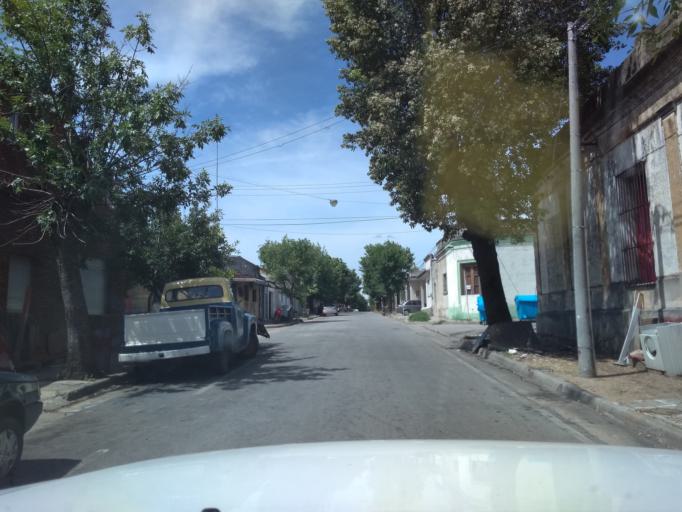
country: UY
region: Florida
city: Florida
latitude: -34.1030
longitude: -56.2148
